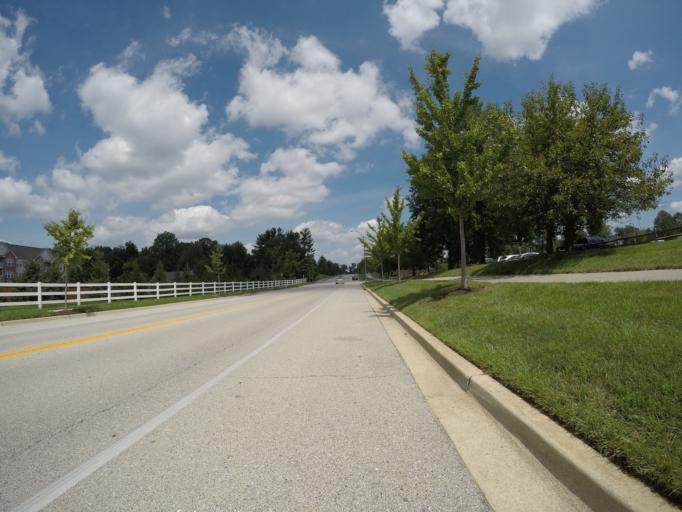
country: US
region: Maryland
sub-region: Anne Arundel County
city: Odenton
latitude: 39.0511
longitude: -76.7049
